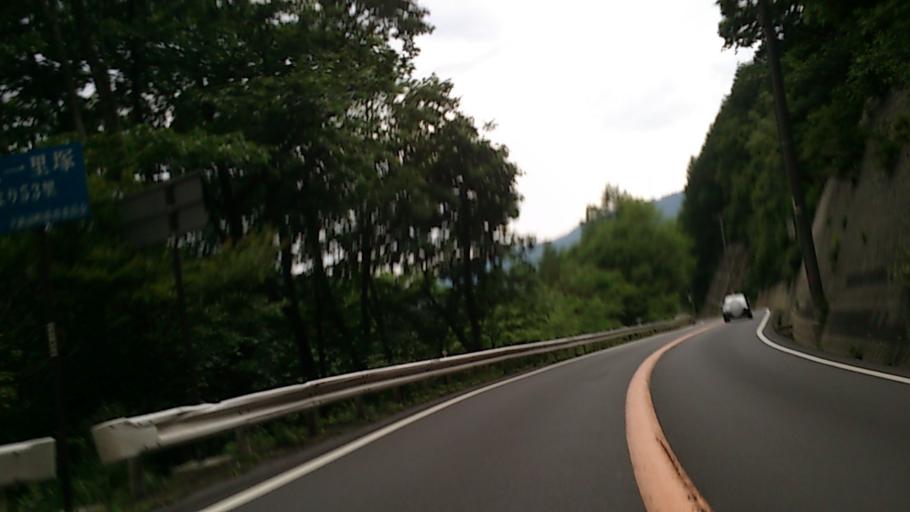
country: JP
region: Nagano
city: Suwa
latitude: 36.1335
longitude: 138.1302
